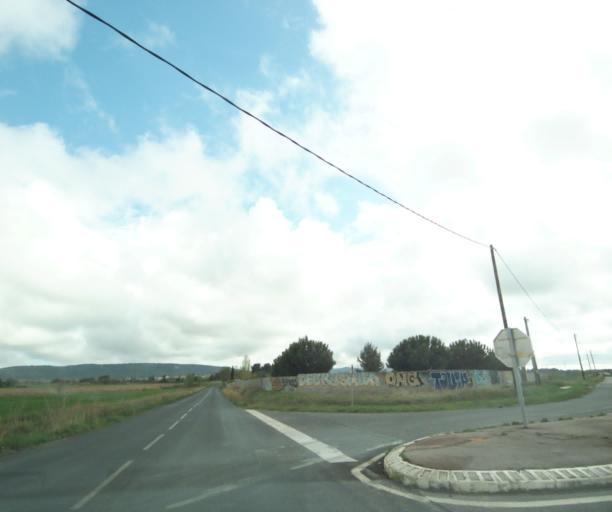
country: FR
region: Languedoc-Roussillon
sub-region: Departement de l'Herault
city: Saussan
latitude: 43.5638
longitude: 3.7752
